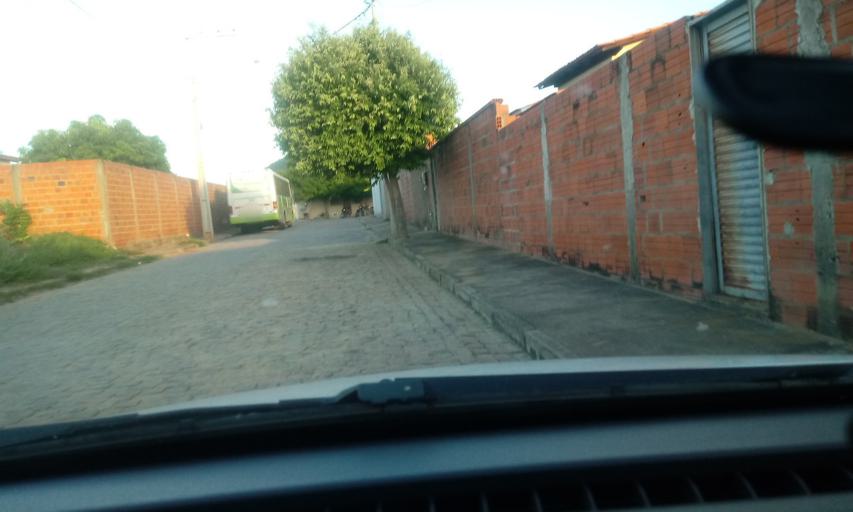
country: BR
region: Bahia
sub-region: Riacho De Santana
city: Riacho de Santana
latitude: -13.9078
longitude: -42.8464
